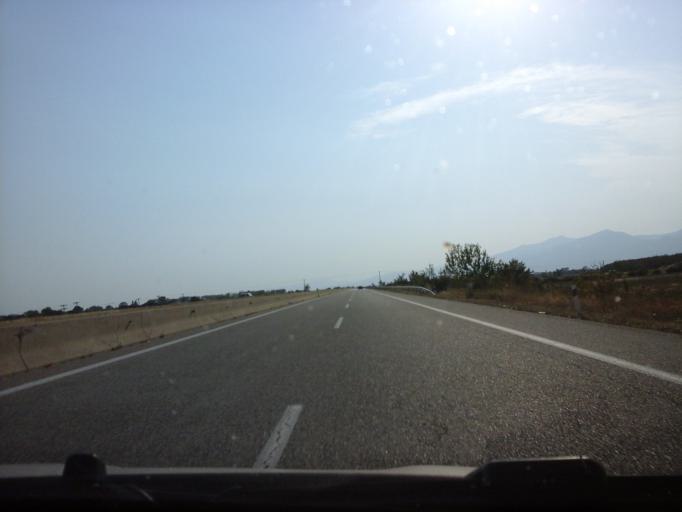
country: GR
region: East Macedonia and Thrace
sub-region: Nomos Xanthis
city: Selero
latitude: 41.1177
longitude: 25.0316
